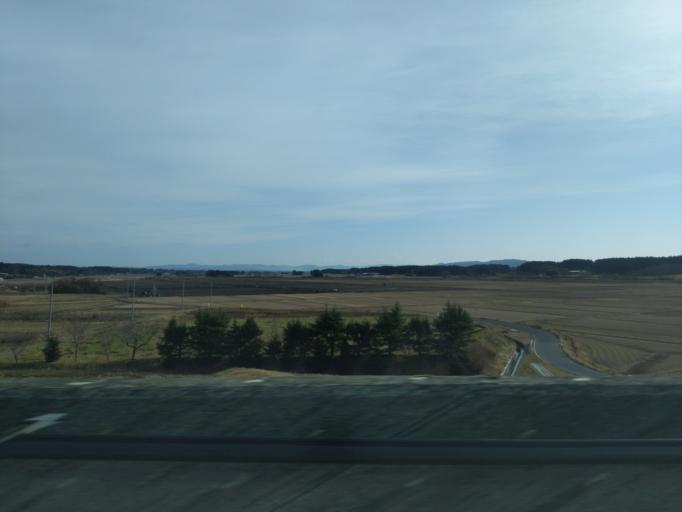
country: JP
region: Miyagi
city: Furukawa
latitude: 38.6552
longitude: 141.0187
